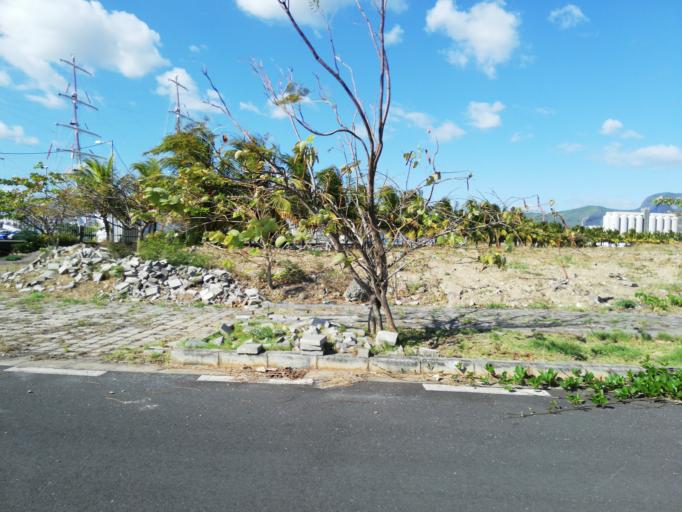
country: MU
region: Port Louis
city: Port Louis
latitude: -20.1569
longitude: 57.4918
